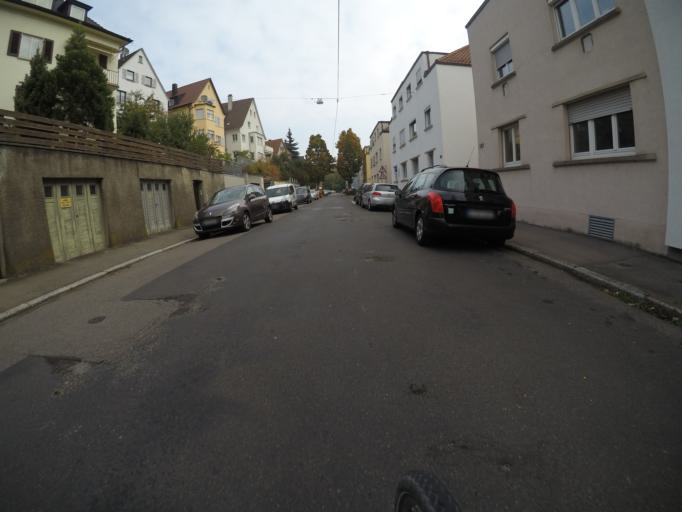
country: DE
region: Baden-Wuerttemberg
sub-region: Regierungsbezirk Stuttgart
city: Stuttgart
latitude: 48.7584
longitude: 9.1481
